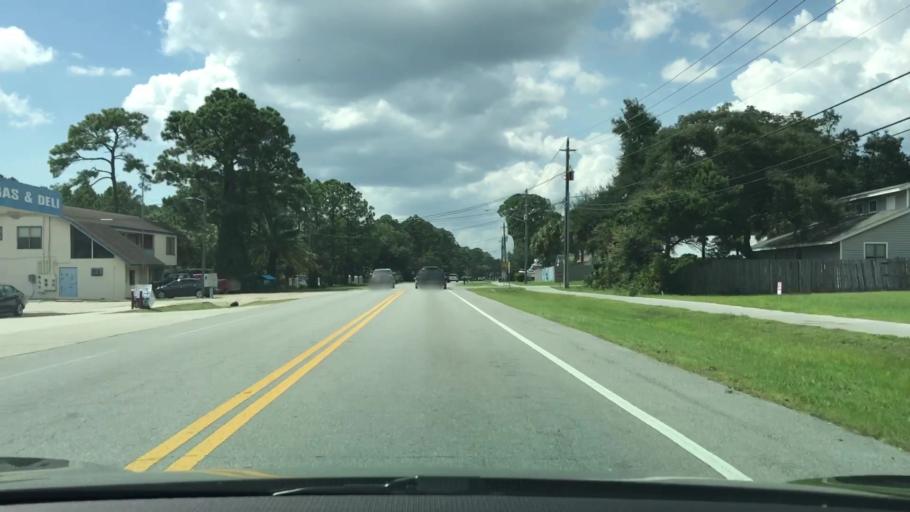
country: US
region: Florida
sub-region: Bay County
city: Lower Grand Lagoon
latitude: 30.1630
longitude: -85.7692
